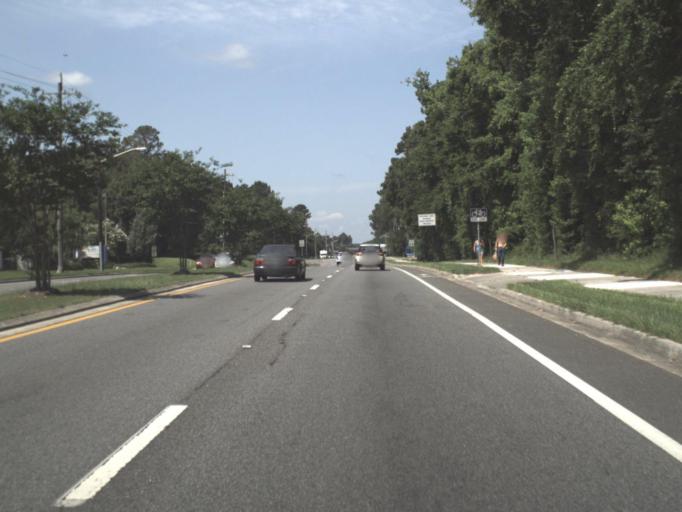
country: US
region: Florida
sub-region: Alachua County
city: Gainesville
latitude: 29.6074
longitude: -82.3660
